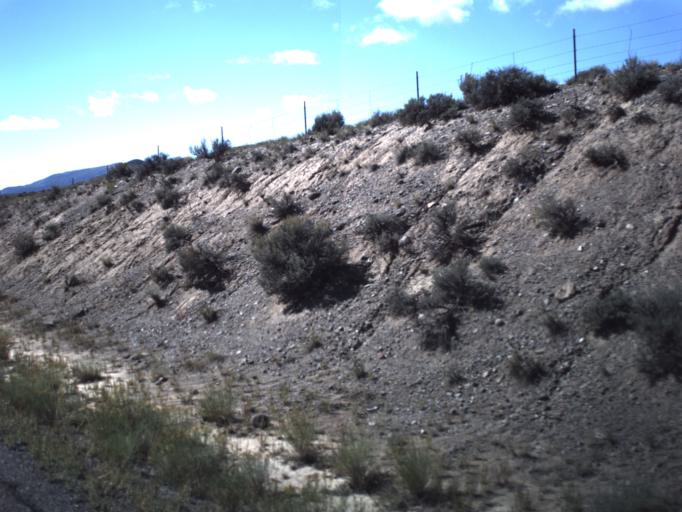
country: US
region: Utah
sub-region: Piute County
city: Junction
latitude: 38.3406
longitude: -111.9528
